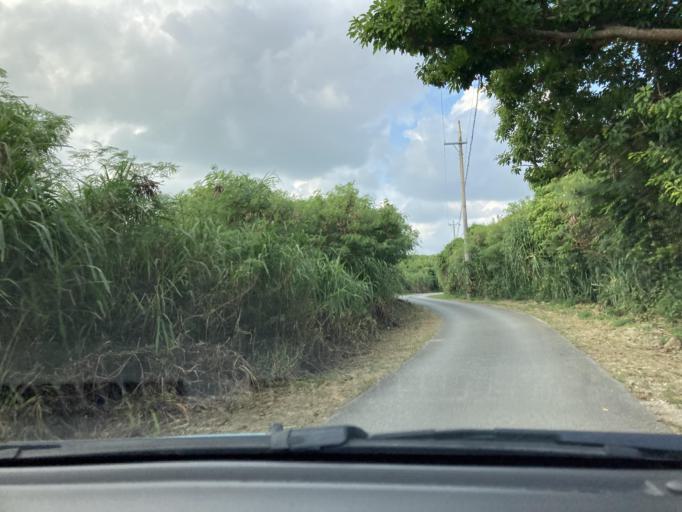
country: JP
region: Okinawa
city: Itoman
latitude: 26.0801
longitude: 127.6687
